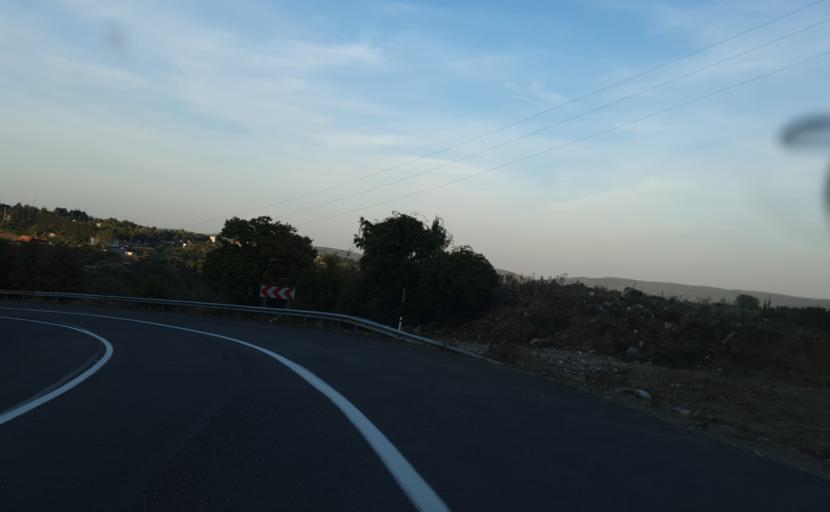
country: TR
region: Kirklareli
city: Sergen
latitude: 41.8152
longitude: 27.7504
